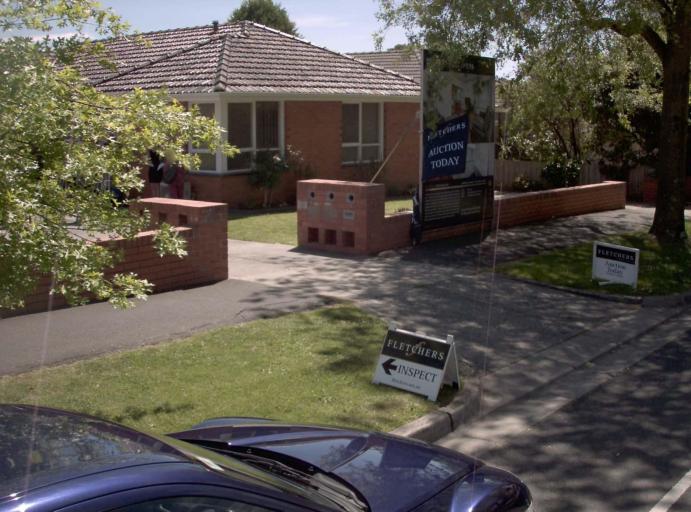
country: AU
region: Victoria
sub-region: Whitehorse
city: Blackburn
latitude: -37.8153
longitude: 145.1567
